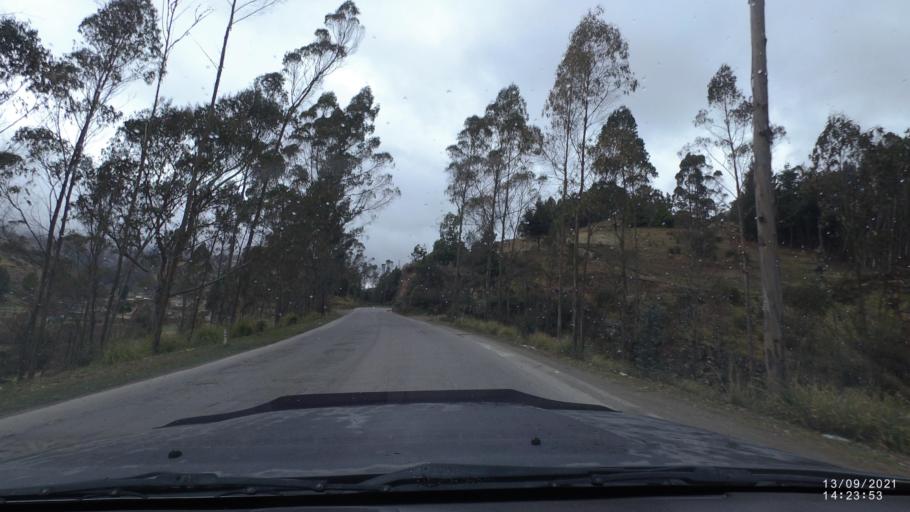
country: BO
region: Cochabamba
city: Colomi
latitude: -17.2794
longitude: -65.8745
